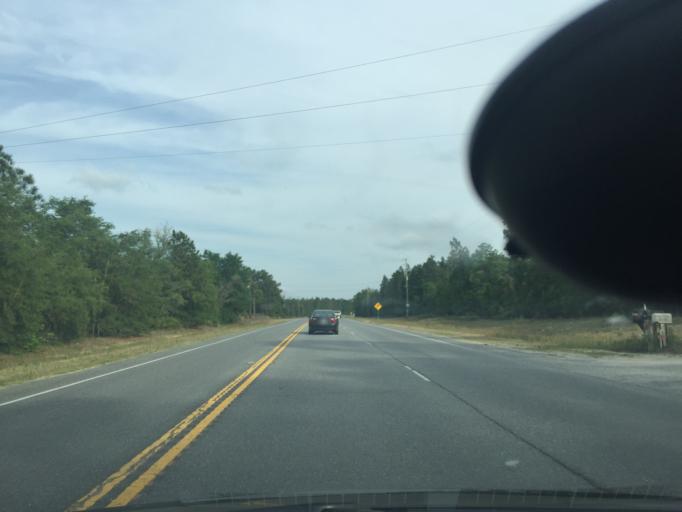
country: US
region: Georgia
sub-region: Chatham County
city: Bloomingdale
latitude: 32.0587
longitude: -81.3501
